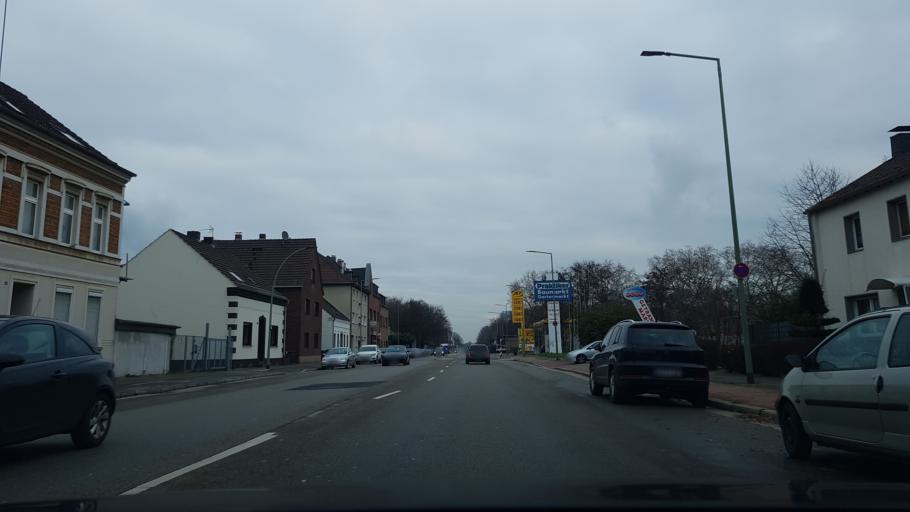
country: DE
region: North Rhine-Westphalia
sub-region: Regierungsbezirk Dusseldorf
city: Moers
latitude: 51.4442
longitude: 6.6848
